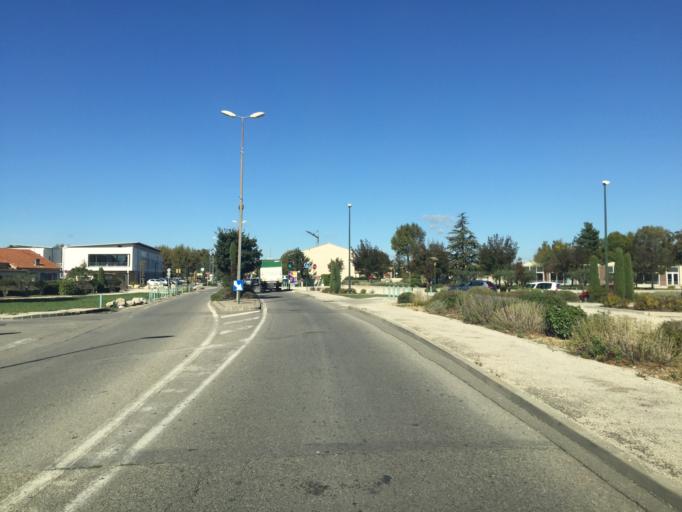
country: FR
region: Provence-Alpes-Cote d'Azur
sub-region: Departement du Vaucluse
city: Vedene
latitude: 43.9787
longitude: 4.9083
